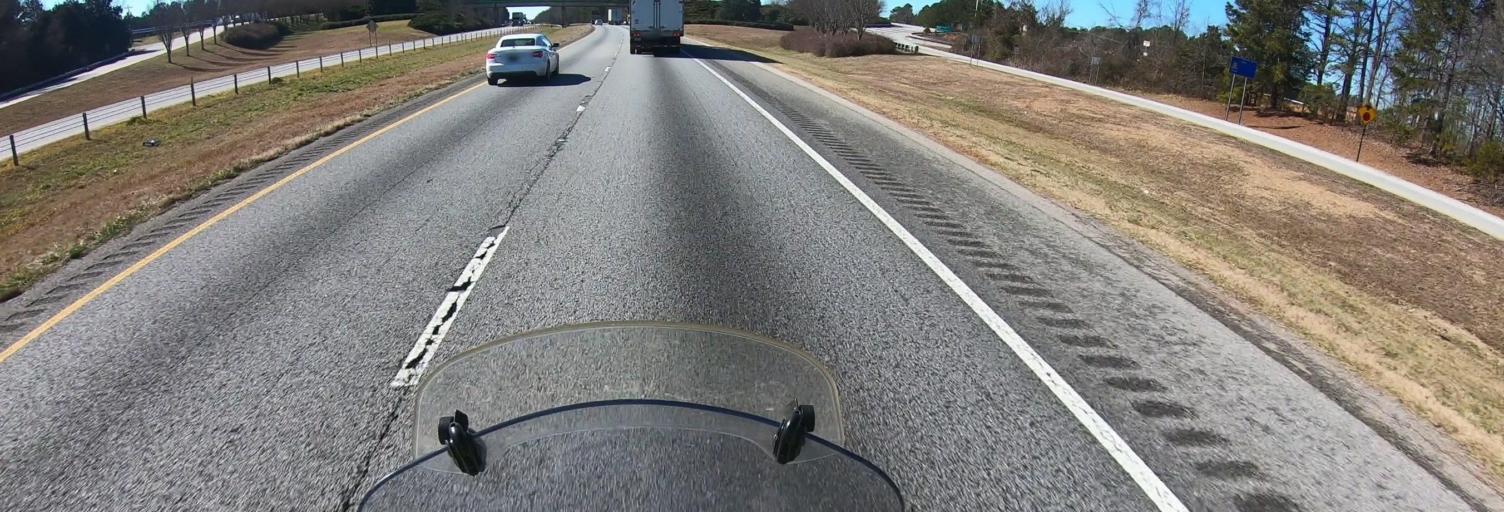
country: US
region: South Carolina
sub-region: Anderson County
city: Centerville
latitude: 34.5483
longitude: -82.8056
